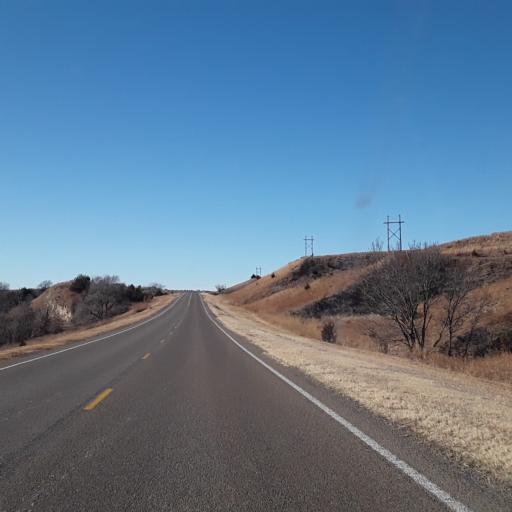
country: US
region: Nebraska
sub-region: Frontier County
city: Stockville
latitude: 40.6295
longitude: -100.5486
